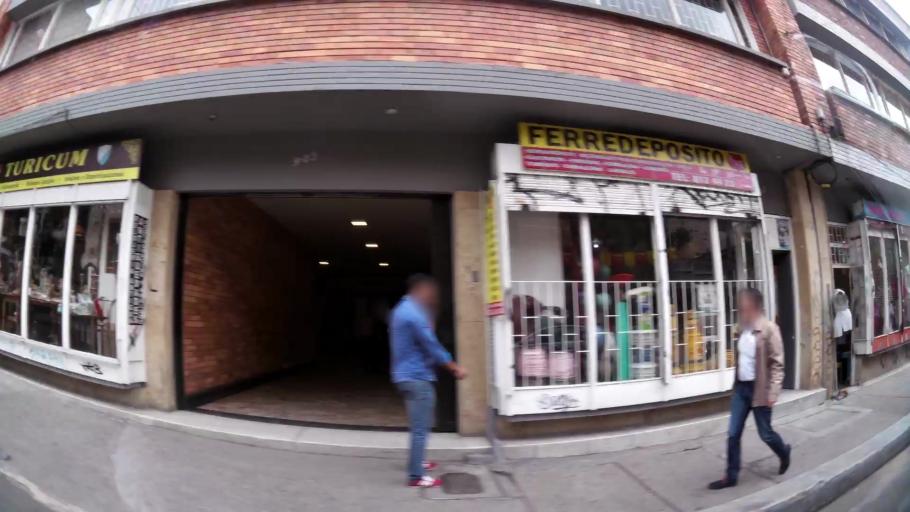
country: CO
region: Bogota D.C.
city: Bogota
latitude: 4.6472
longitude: -74.0625
